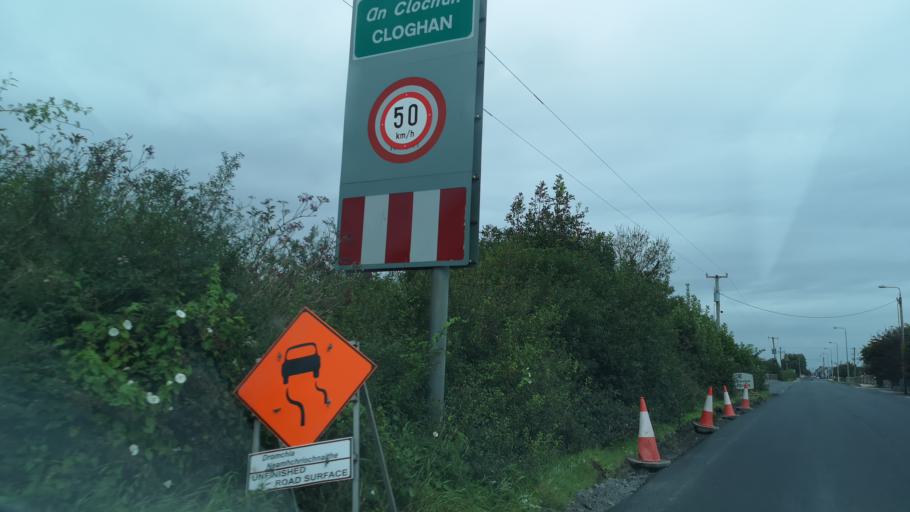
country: IE
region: Leinster
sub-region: Uibh Fhaili
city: Ferbane
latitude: 53.2203
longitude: -7.8904
